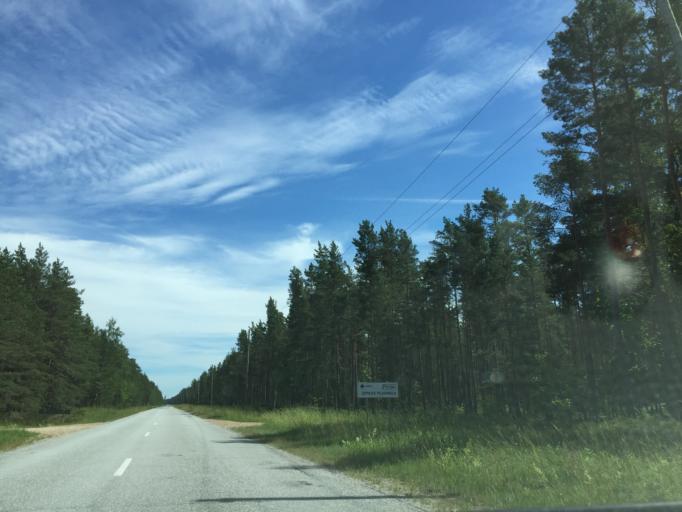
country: LV
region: Rojas
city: Roja
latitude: 57.5625
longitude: 22.6586
